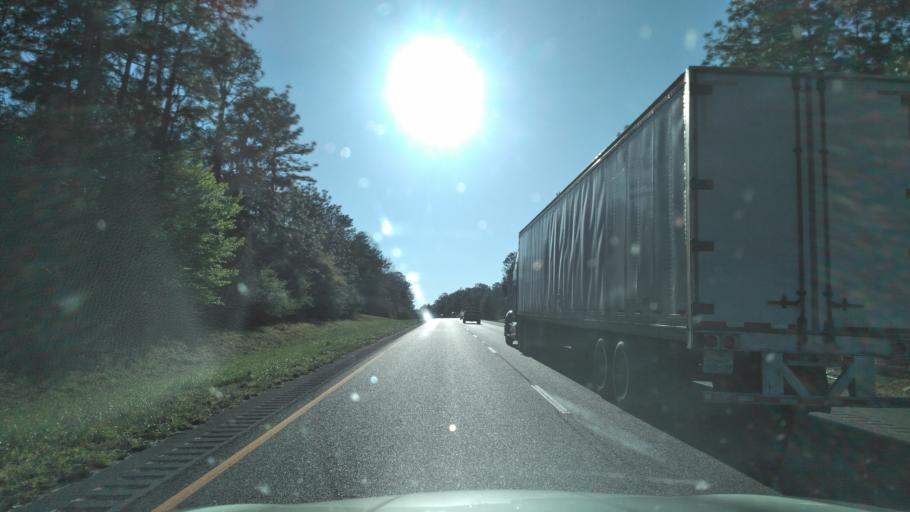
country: US
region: Alabama
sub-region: Escambia County
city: Atmore
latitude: 31.0628
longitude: -87.5716
